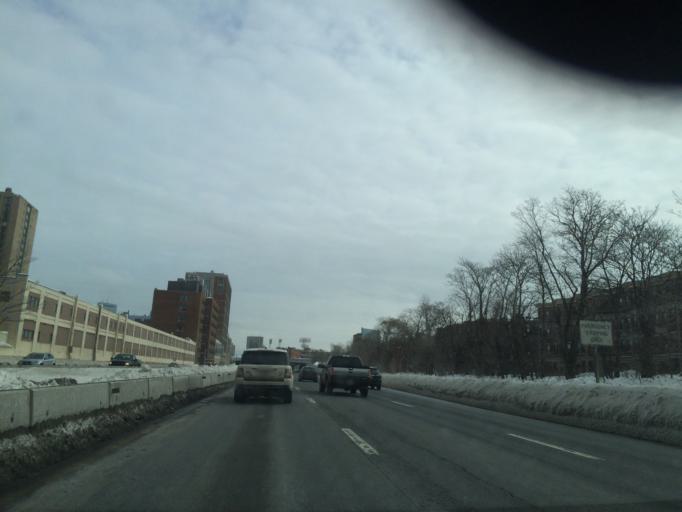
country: US
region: Massachusetts
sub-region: Norfolk County
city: Brookline
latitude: 42.3488
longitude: -71.1062
